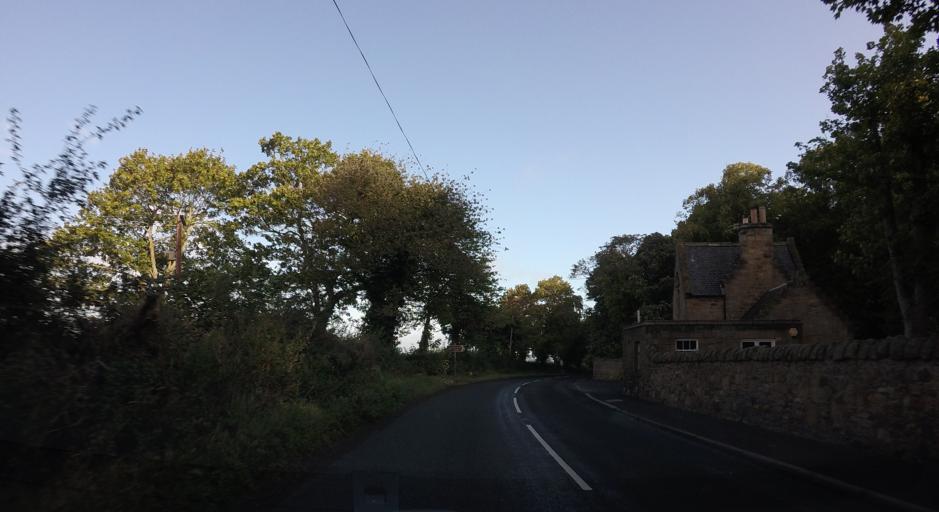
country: GB
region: Scotland
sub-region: East Lothian
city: Musselburgh
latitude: 55.9150
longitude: -3.0264
